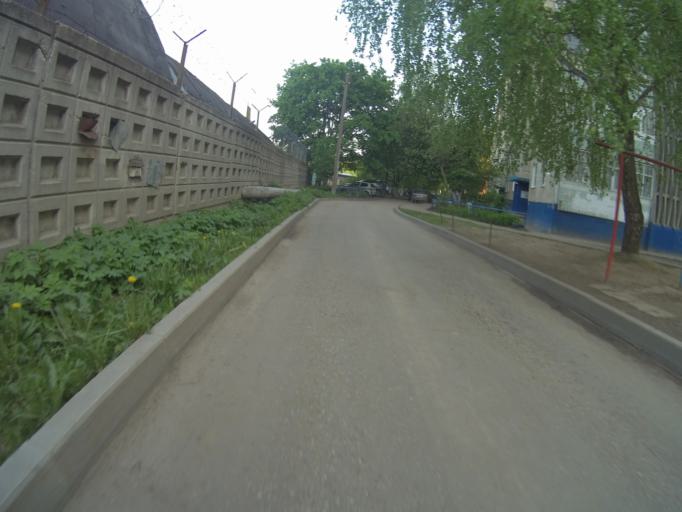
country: RU
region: Vladimir
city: Kommunar
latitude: 56.1703
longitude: 40.4553
